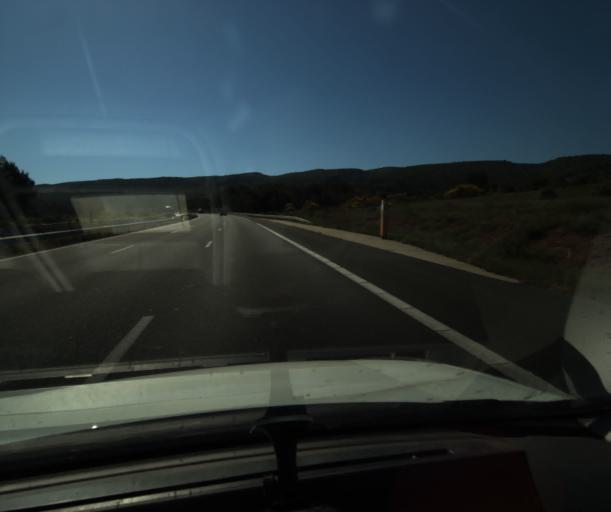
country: FR
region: Languedoc-Roussillon
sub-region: Departement de l'Aude
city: Capendu
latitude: 43.1731
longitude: 2.6020
